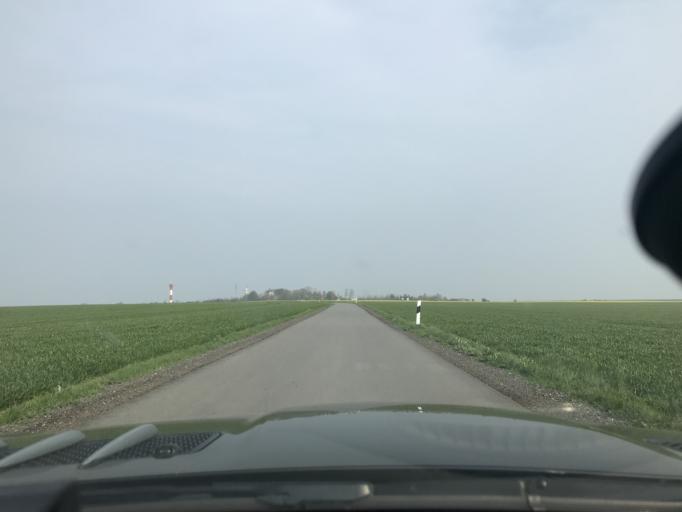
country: DE
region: Schleswig-Holstein
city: Fehmarn
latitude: 54.4935
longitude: 11.2247
